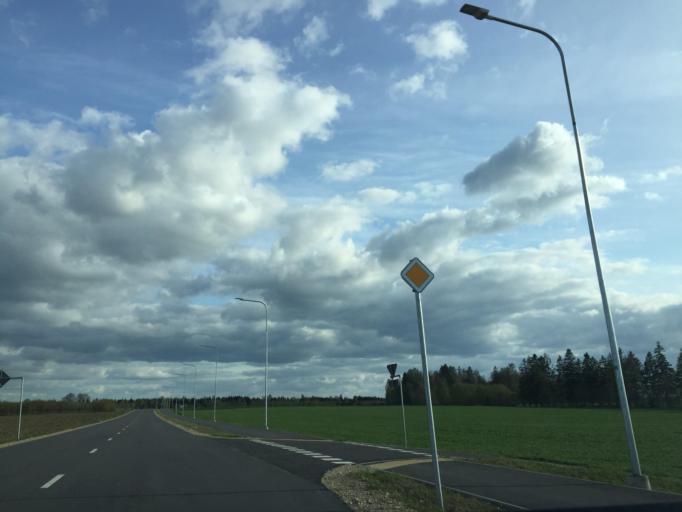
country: LV
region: Sigulda
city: Sigulda
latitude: 57.1397
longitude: 24.8610
